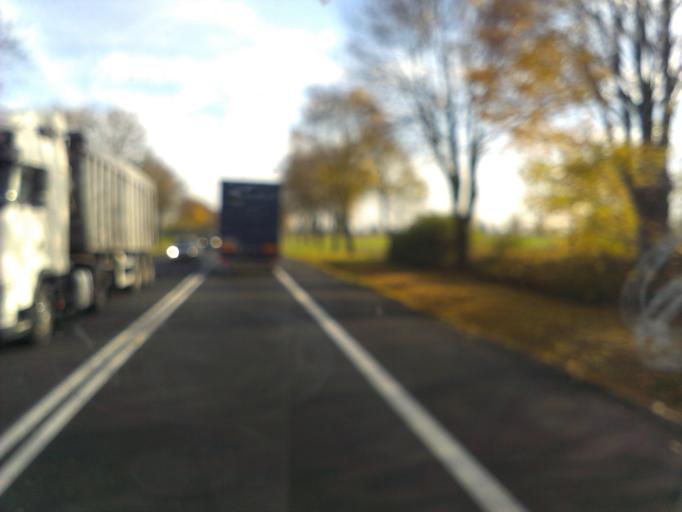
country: PL
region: Lower Silesian Voivodeship
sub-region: Powiat polkowicki
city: Gaworzyce
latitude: 51.6233
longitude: 15.9185
